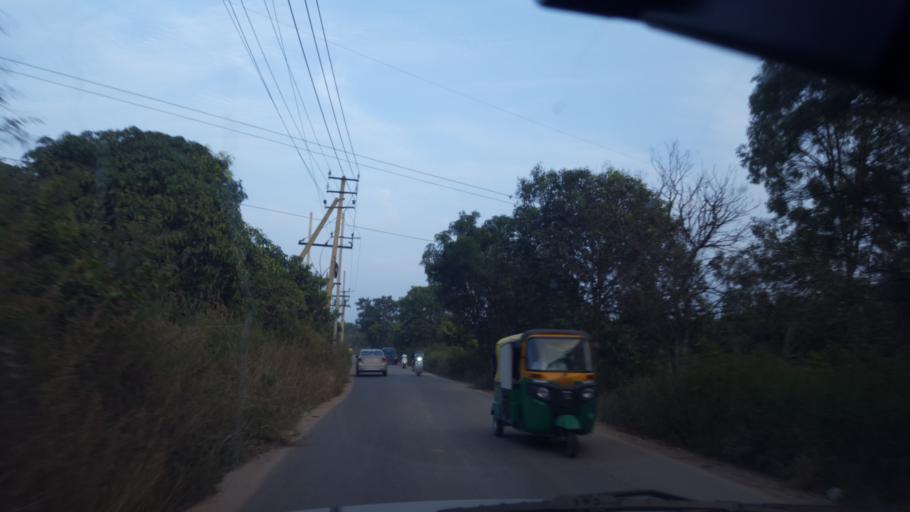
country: IN
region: Karnataka
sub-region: Bangalore Rural
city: Hoskote
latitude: 13.0772
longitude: 77.6983
